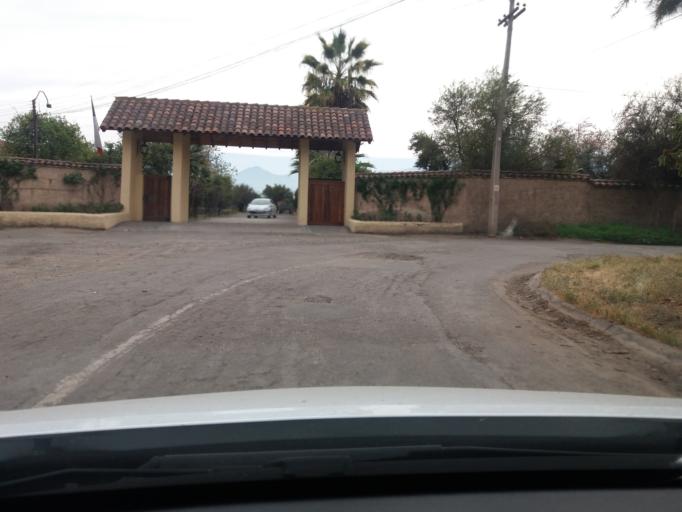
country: CL
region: Valparaiso
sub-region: Provincia de Los Andes
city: Los Andes
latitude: -32.8241
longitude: -70.6474
